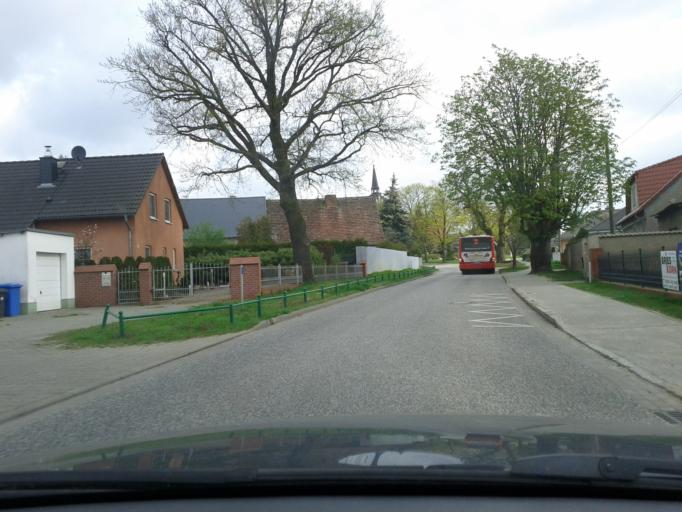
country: DE
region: Brandenburg
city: Schoneiche
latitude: 52.4900
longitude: 13.6714
